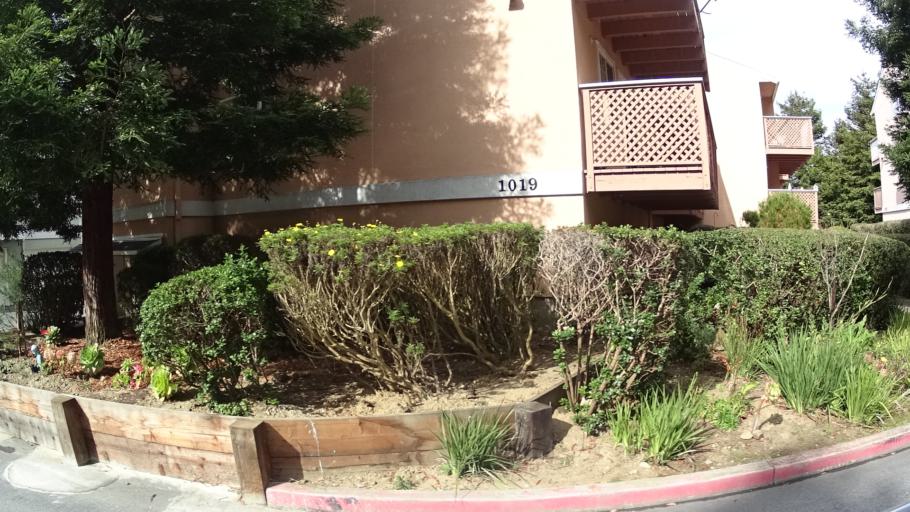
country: US
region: California
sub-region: San Mateo County
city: Daly City
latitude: 37.7056
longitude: -122.4415
